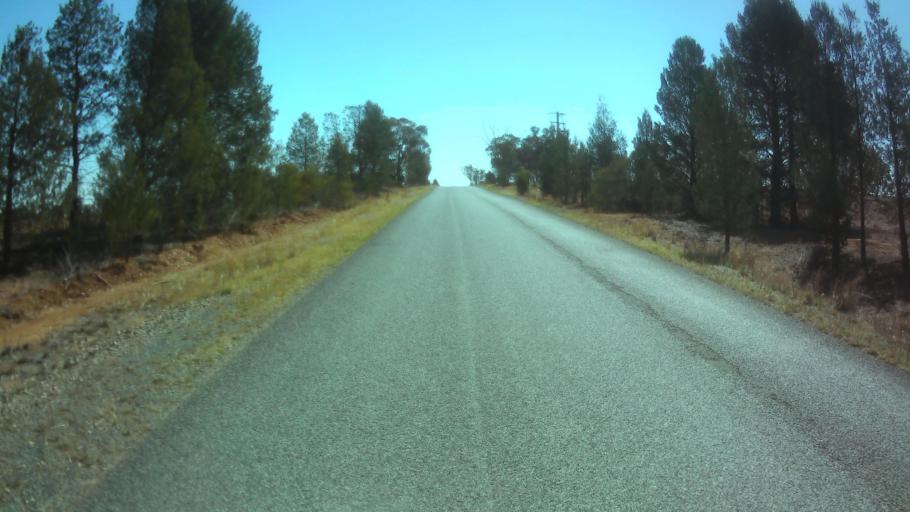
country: AU
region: New South Wales
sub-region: Weddin
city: Grenfell
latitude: -33.7534
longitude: 147.8409
